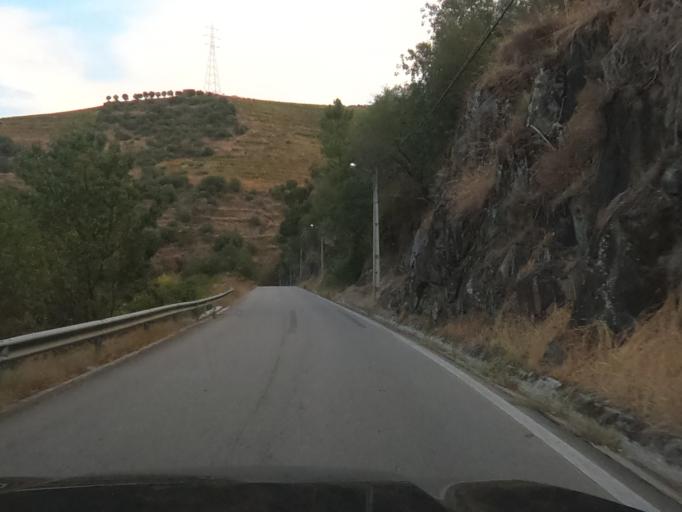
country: PT
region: Vila Real
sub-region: Peso da Regua
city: Peso da Regua
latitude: 41.1651
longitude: -7.7656
